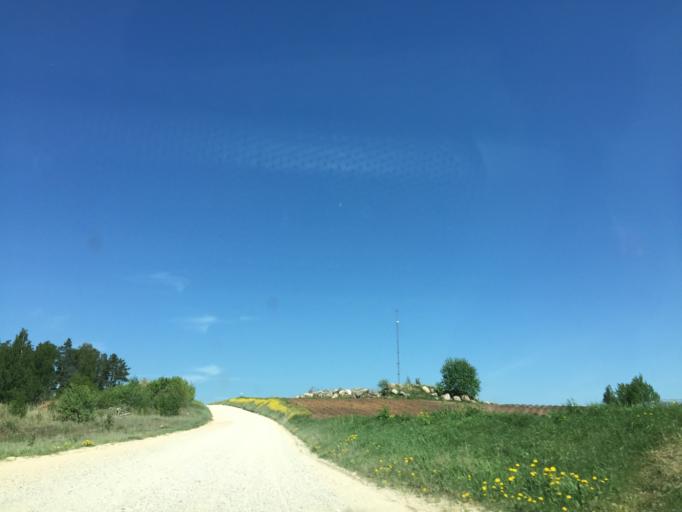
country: LV
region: Ikskile
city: Ikskile
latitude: 56.8643
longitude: 24.5020
